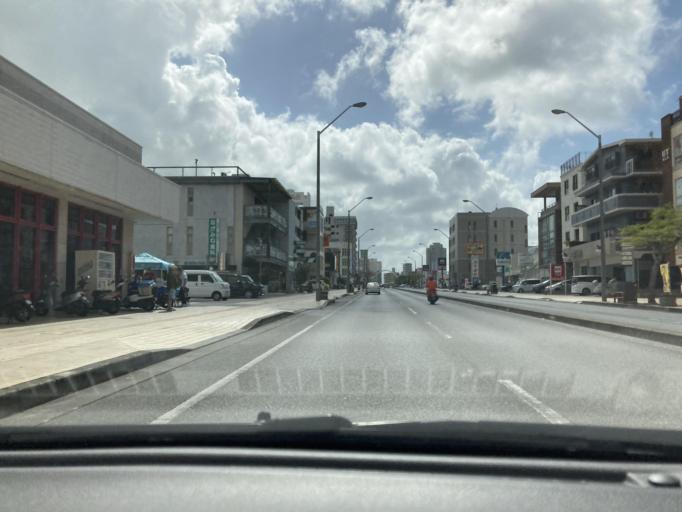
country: JP
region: Okinawa
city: Naha-shi
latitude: 26.2305
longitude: 127.6996
